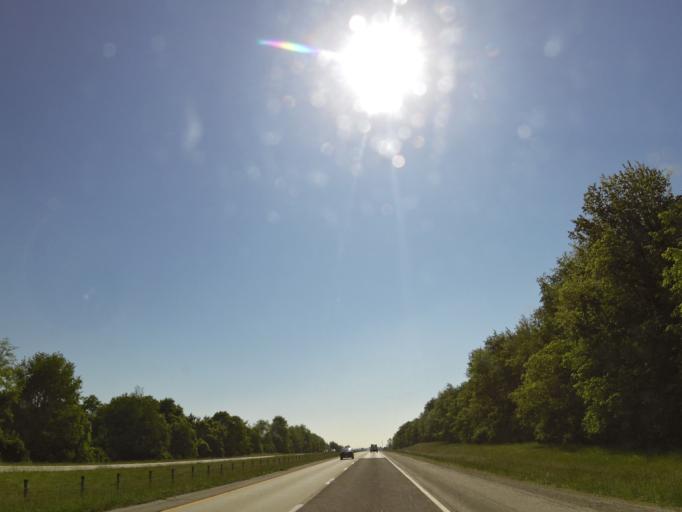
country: US
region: Kentucky
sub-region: Woodford County
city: Midway
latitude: 38.1624
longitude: -84.7274
